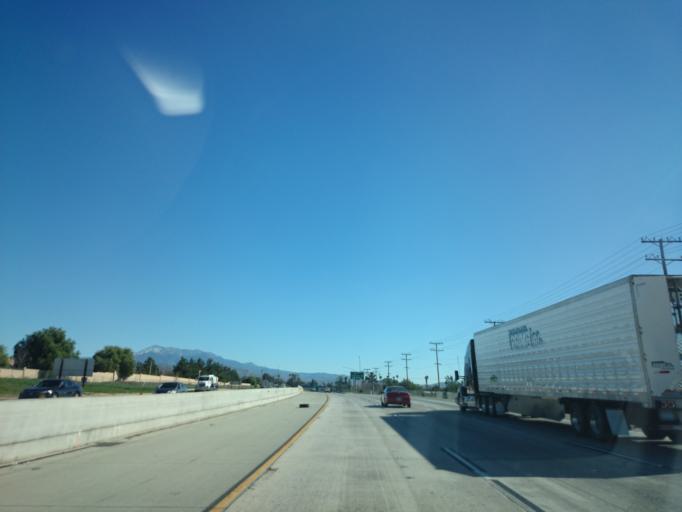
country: US
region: California
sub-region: Riverside County
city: Beaumont
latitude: 33.9375
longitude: -116.9967
